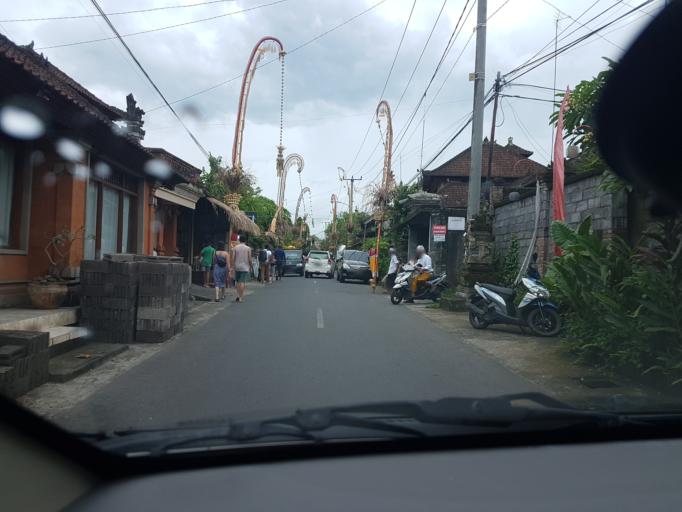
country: ID
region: Bali
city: Banjar Pande
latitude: -8.5052
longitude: 115.2477
